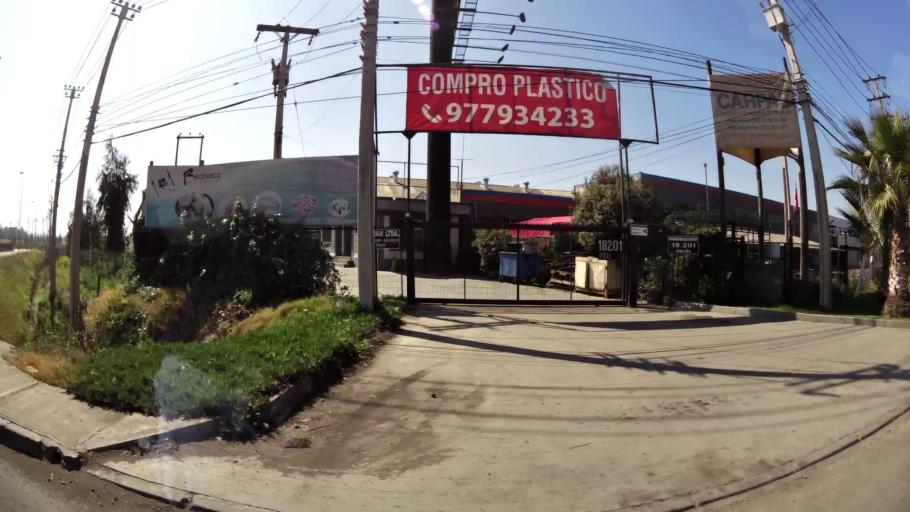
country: CL
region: Santiago Metropolitan
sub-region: Provincia de Chacabuco
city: Chicureo Abajo
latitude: -33.3012
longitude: -70.7289
